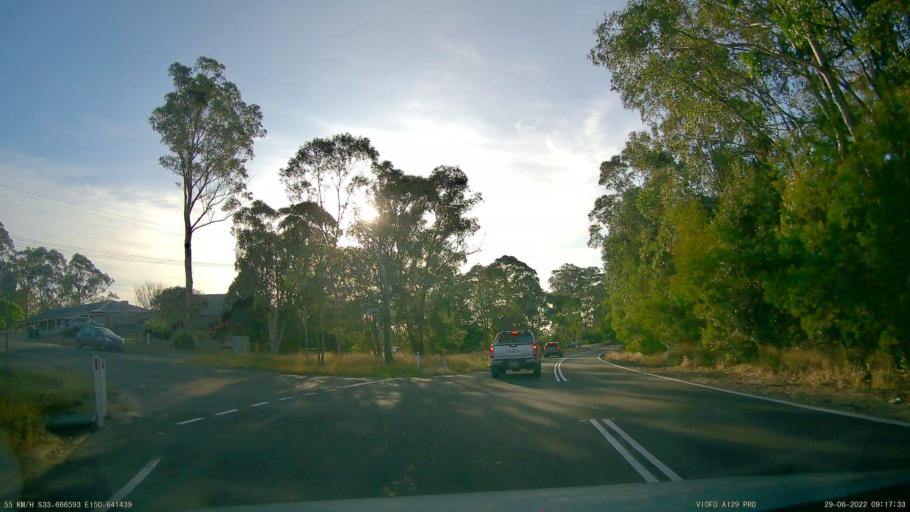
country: AU
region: New South Wales
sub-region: Penrith Municipality
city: Emu Heights
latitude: -33.6665
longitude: 150.6418
